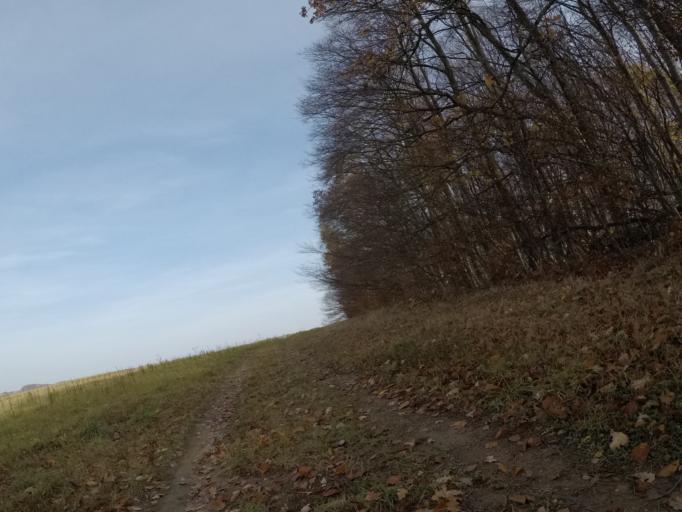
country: SK
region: Presovsky
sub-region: Okres Presov
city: Presov
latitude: 48.9158
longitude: 21.2174
